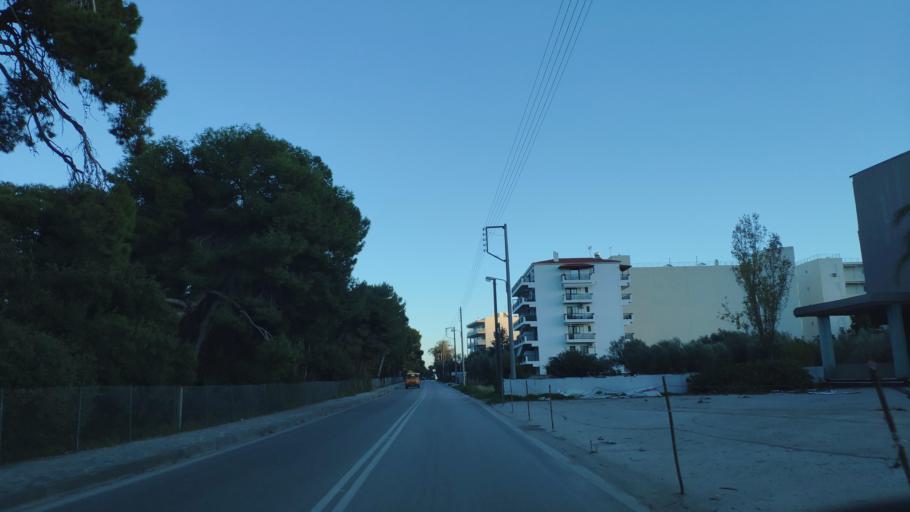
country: GR
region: Peloponnese
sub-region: Nomos Korinthias
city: Xylokastro
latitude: 38.0715
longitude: 22.6483
